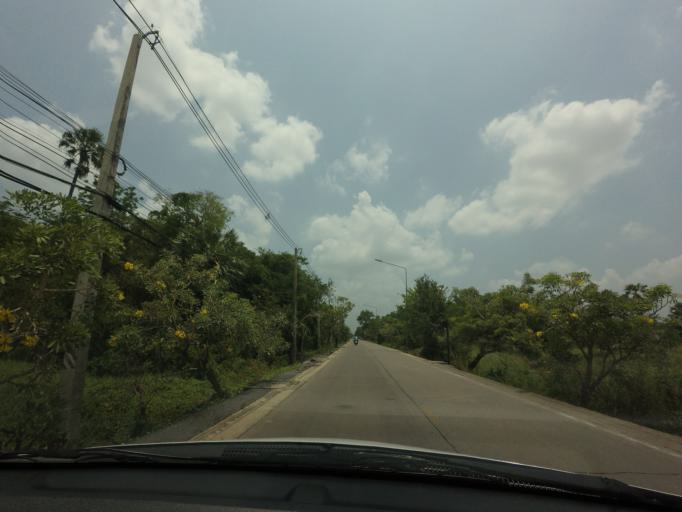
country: TH
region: Pathum Thani
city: Pathum Thani
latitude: 14.0429
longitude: 100.5507
